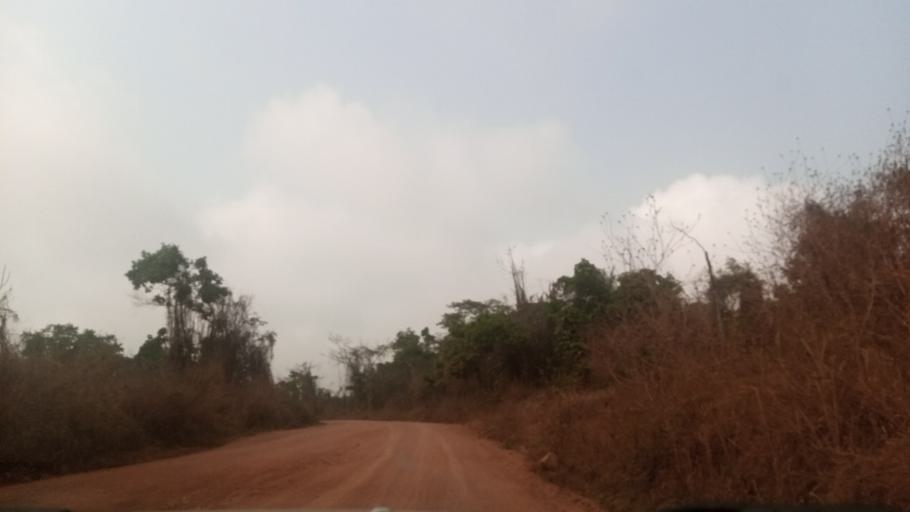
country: NG
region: Osun
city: Modakeke
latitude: 7.1281
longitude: 4.4094
